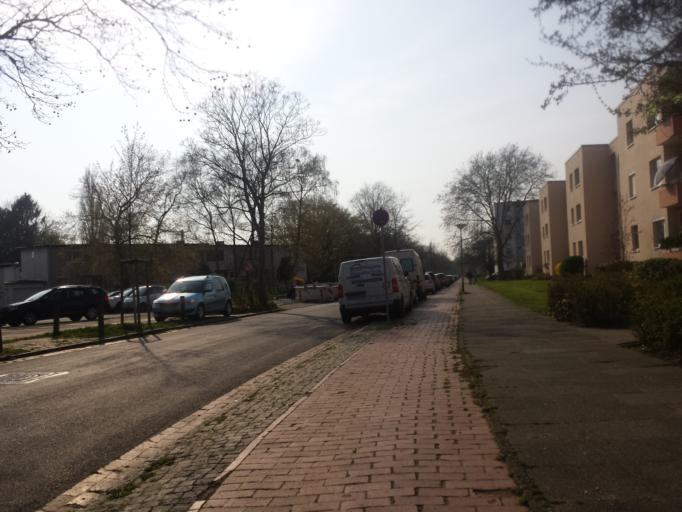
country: DE
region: Lower Saxony
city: Lilienthal
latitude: 53.0762
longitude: 8.9108
